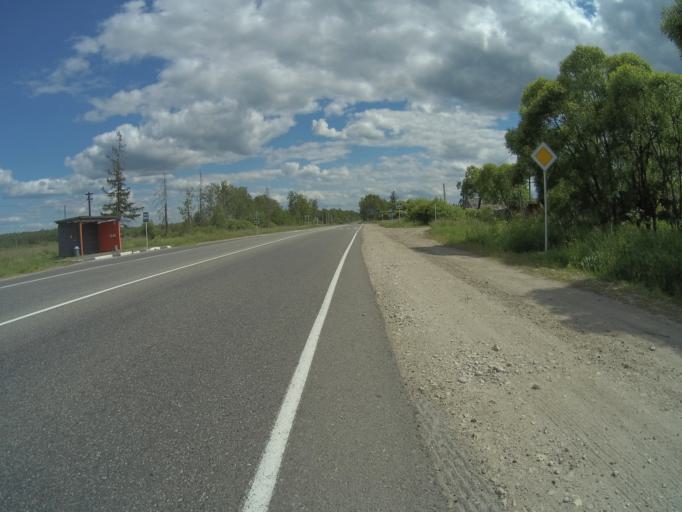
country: RU
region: Vladimir
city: Kommunar
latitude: 56.0385
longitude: 40.5520
